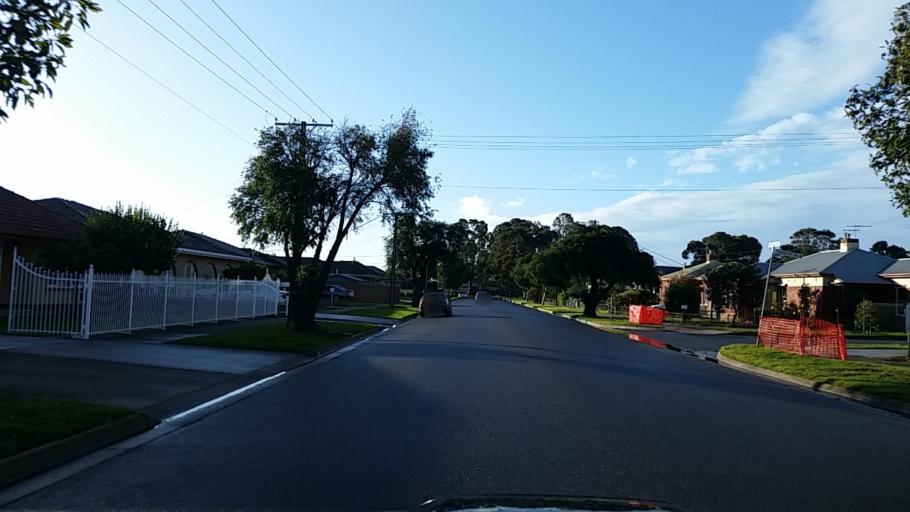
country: AU
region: South Australia
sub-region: Charles Sturt
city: Findon
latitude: -34.9004
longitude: 138.5368
